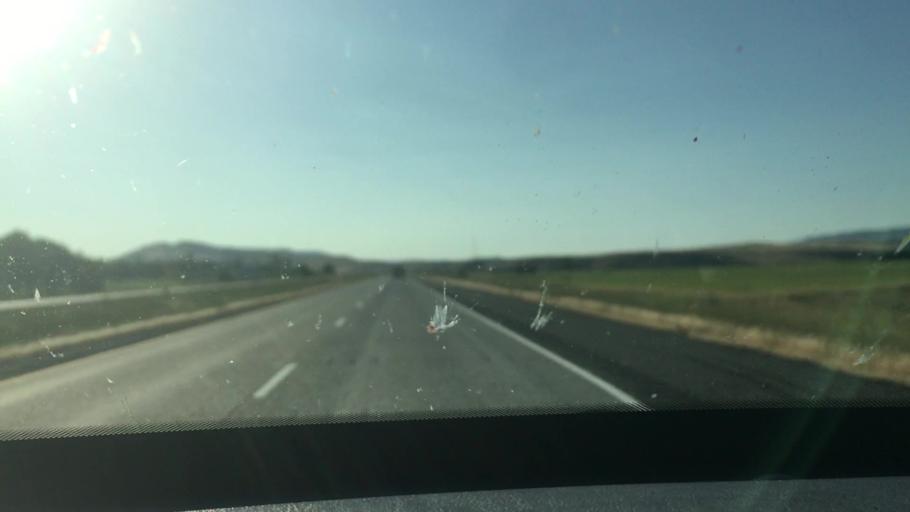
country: US
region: Washington
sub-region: Kittitas County
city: Ellensburg
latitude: 47.0710
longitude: -120.7082
